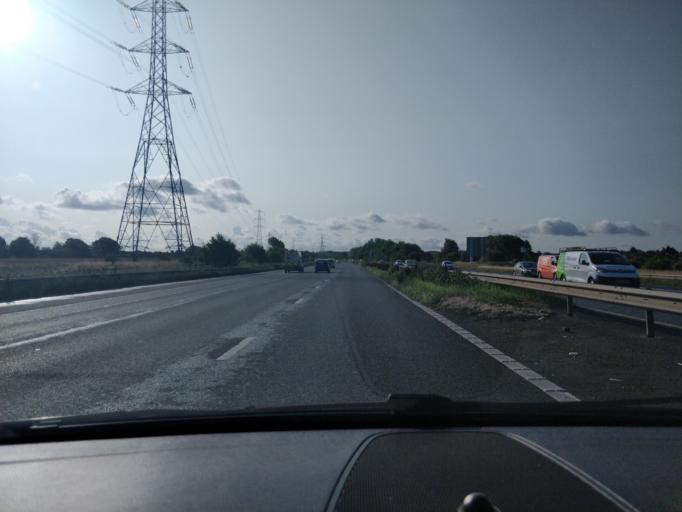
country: GB
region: England
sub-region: Sefton
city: Melling
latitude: 53.4884
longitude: -2.9386
